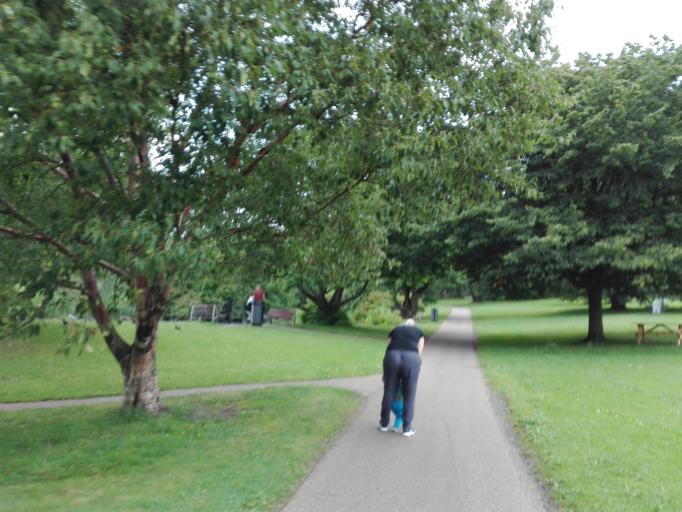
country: DK
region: Central Jutland
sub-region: Arhus Kommune
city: Arhus
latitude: 56.1624
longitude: 10.1882
